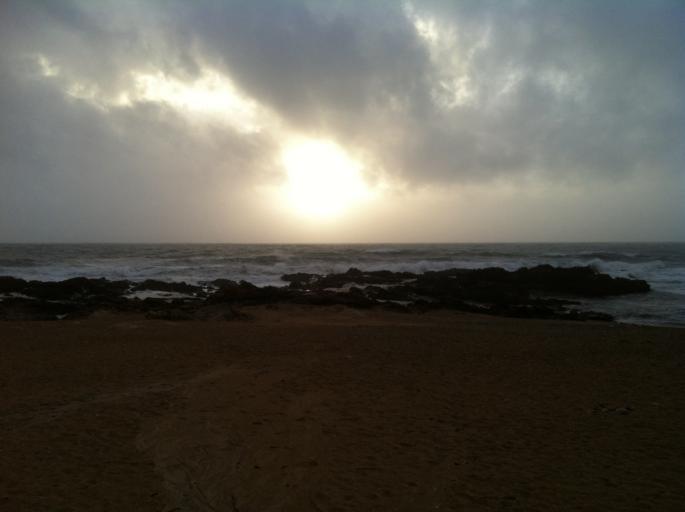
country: PT
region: Porto
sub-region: Matosinhos
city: Matosinhos
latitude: 41.1673
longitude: -8.6896
